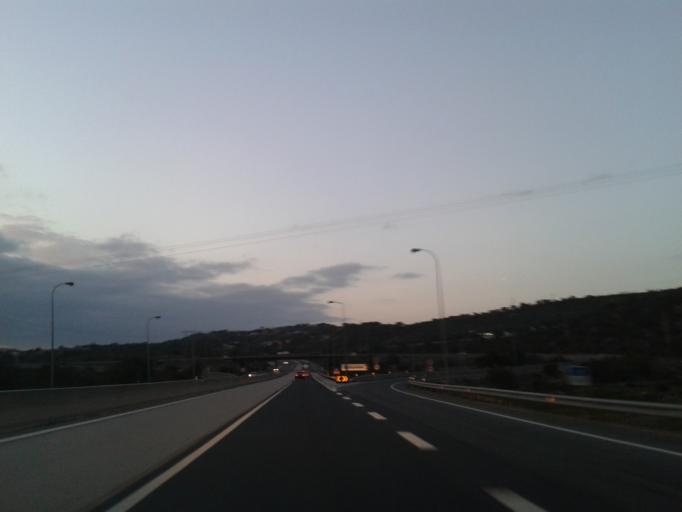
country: PT
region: Faro
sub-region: Loule
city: Boliqueime
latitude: 37.1447
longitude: -8.1226
